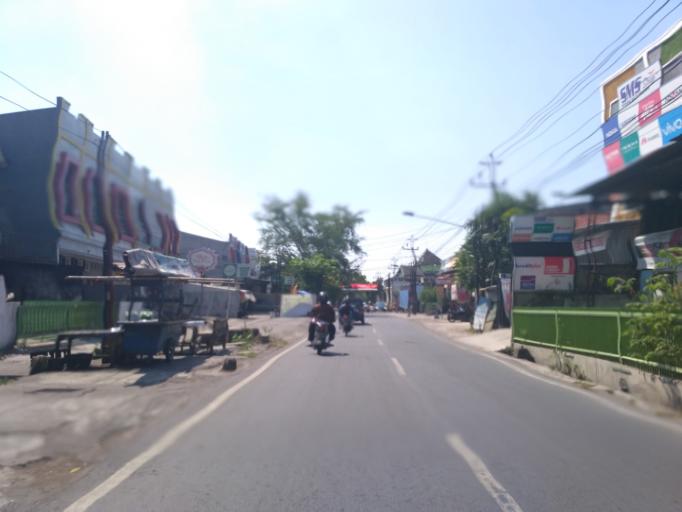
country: ID
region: Central Java
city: Semarang
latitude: -7.0076
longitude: 110.4425
